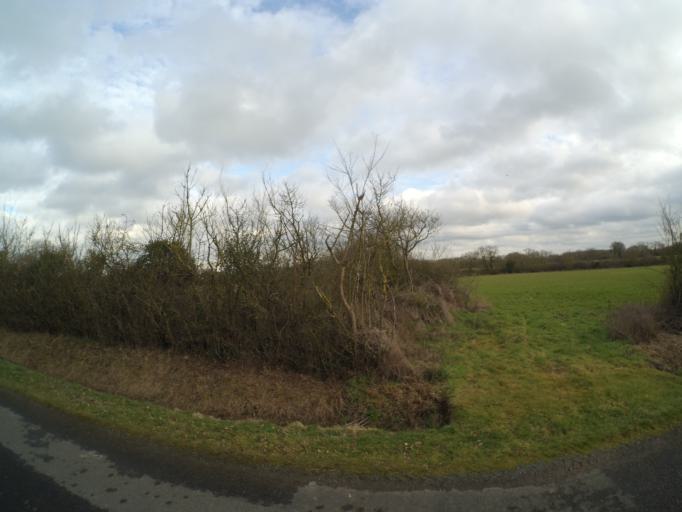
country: FR
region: Pays de la Loire
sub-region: Departement de la Loire-Atlantique
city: Saint-Hilaire-de-Clisson
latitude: 47.0447
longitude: -1.2915
